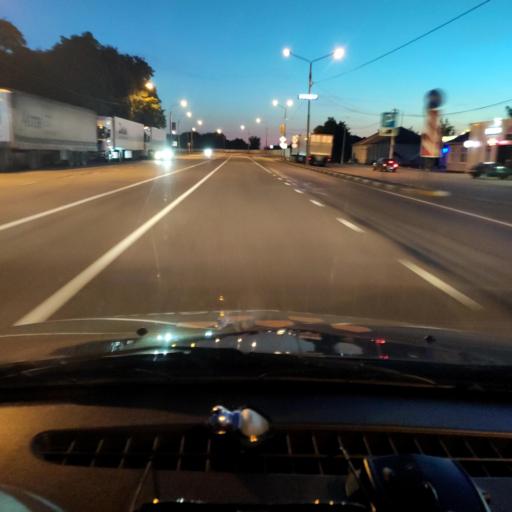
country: RU
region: Belgorod
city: Skorodnoye
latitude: 51.1867
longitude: 37.3698
